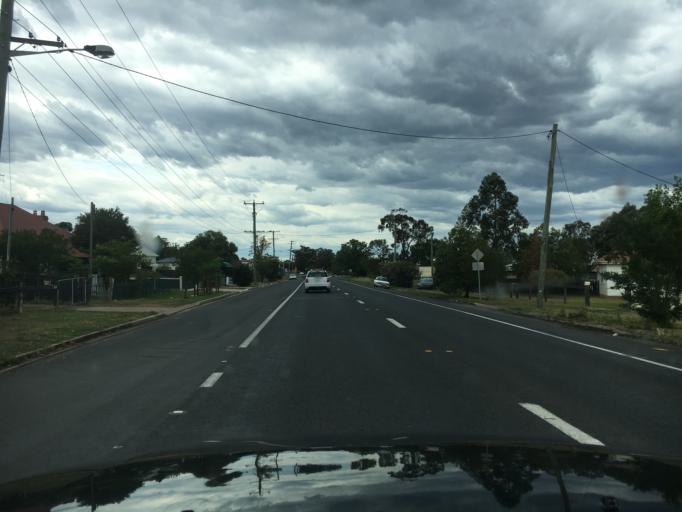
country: AU
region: New South Wales
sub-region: Muswellbrook
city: Muswellbrook
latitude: -32.0412
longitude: 150.8652
